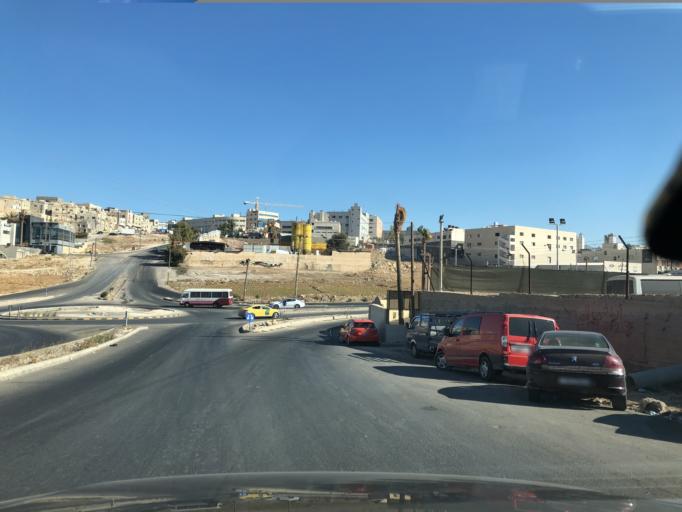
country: JO
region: Amman
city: Wadi as Sir
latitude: 31.9333
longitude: 35.8454
